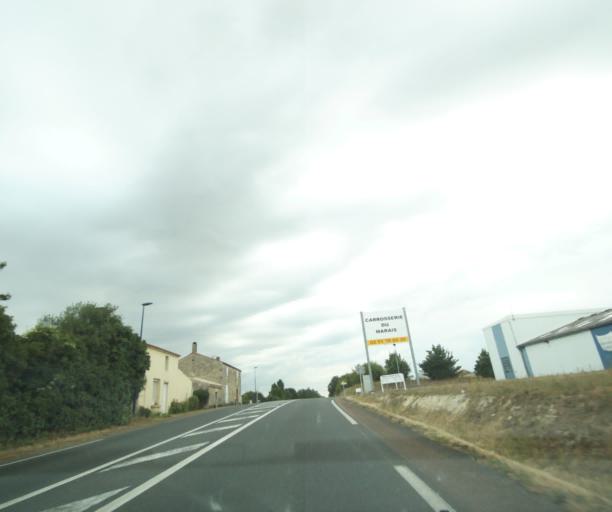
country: FR
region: Pays de la Loire
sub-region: Departement de la Vendee
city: Chaille-les-Marais
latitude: 46.4004
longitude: -1.0319
